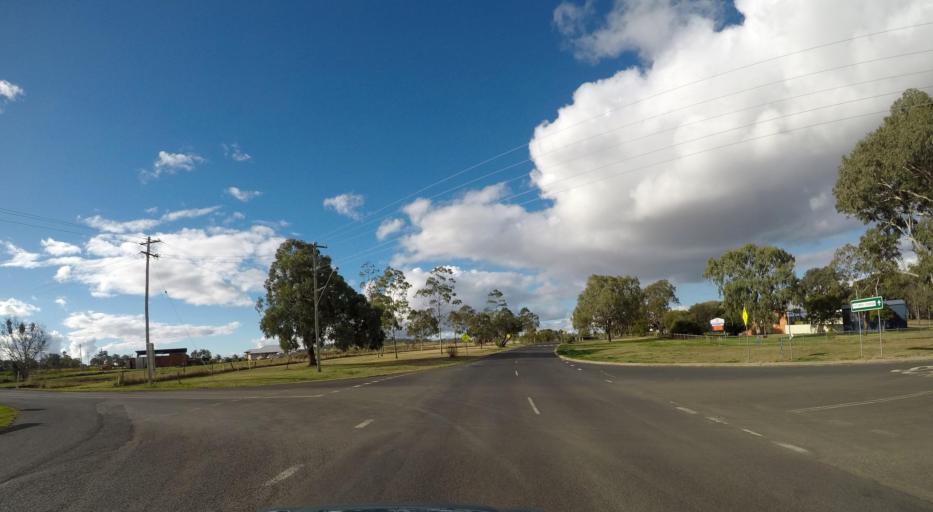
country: AU
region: Queensland
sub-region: Toowoomba
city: Westbrook
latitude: -27.7099
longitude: 151.6433
